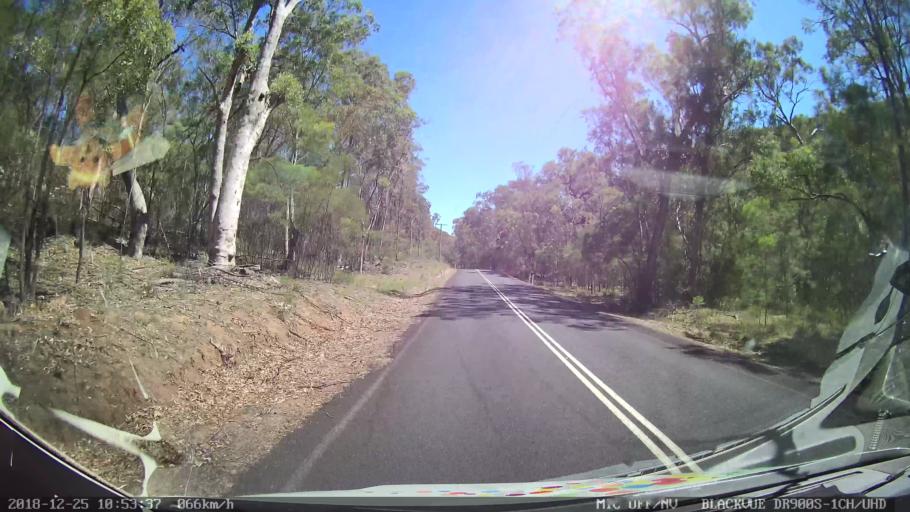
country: AU
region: New South Wales
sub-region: Upper Hunter Shire
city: Merriwa
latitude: -32.4184
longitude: 150.2732
